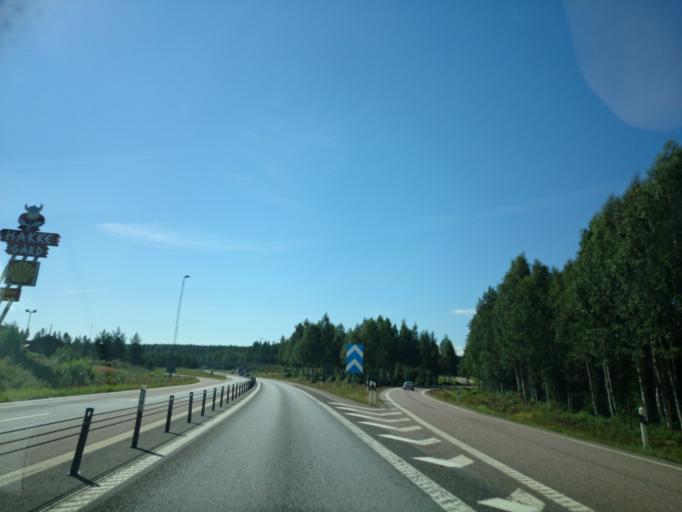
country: SE
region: Gaevleborg
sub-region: Gavle Kommun
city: Norrsundet
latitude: 60.9048
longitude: 17.0155
